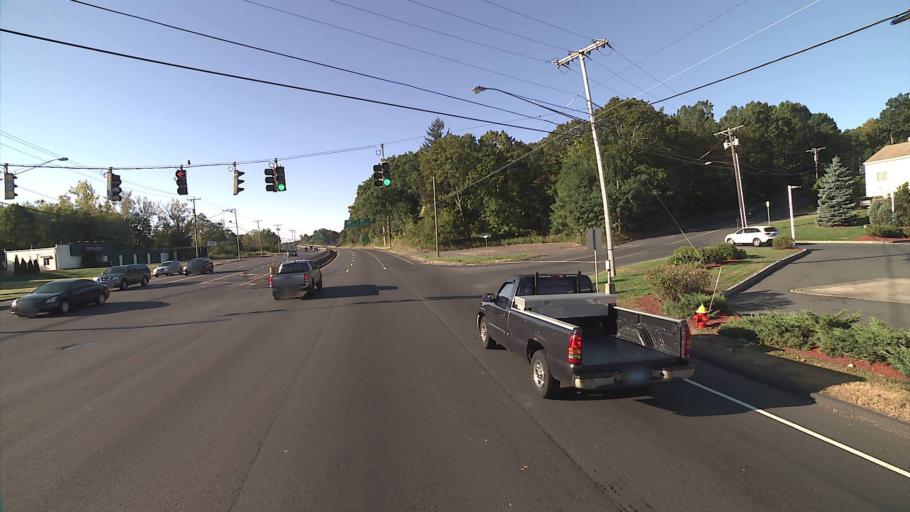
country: US
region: Connecticut
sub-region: Hartford County
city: Newington
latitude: 41.7035
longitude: -72.7029
